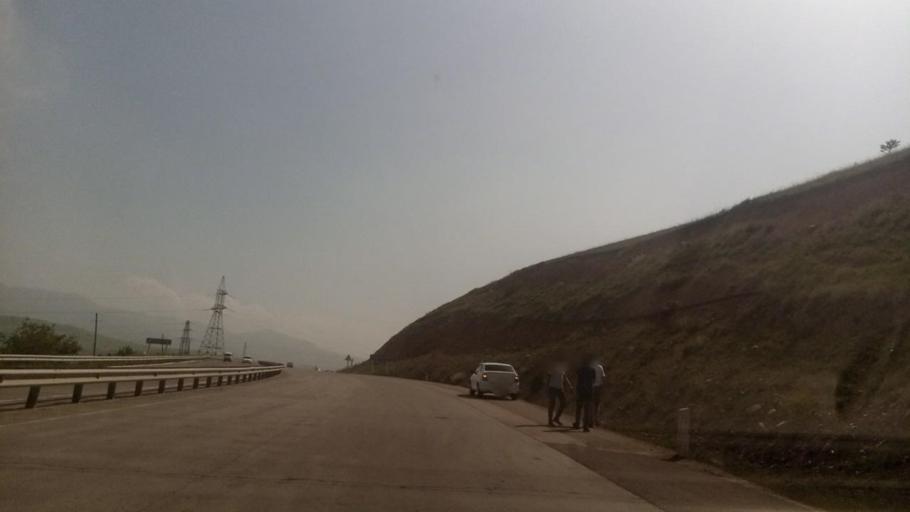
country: UZ
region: Toshkent
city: Angren
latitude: 41.0707
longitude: 70.2327
